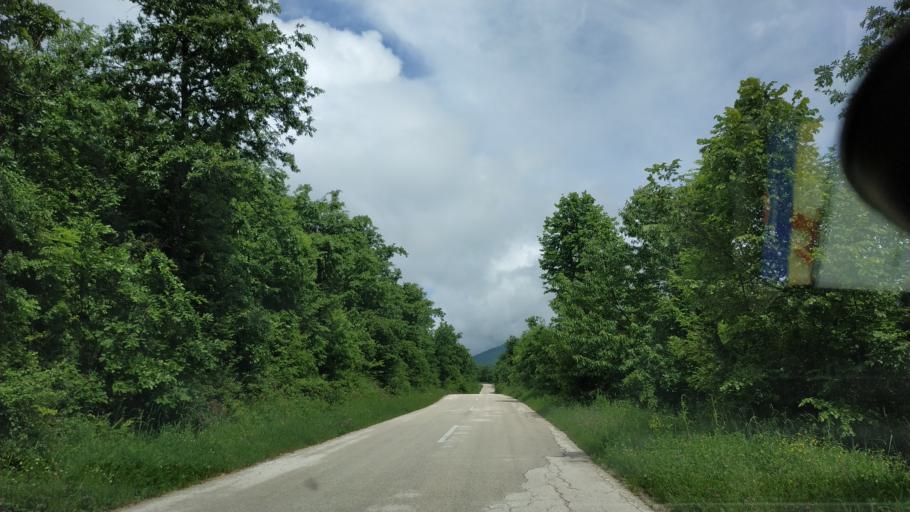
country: RS
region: Central Serbia
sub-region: Zajecarski Okrug
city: Boljevac
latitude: 43.7330
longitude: 21.9533
